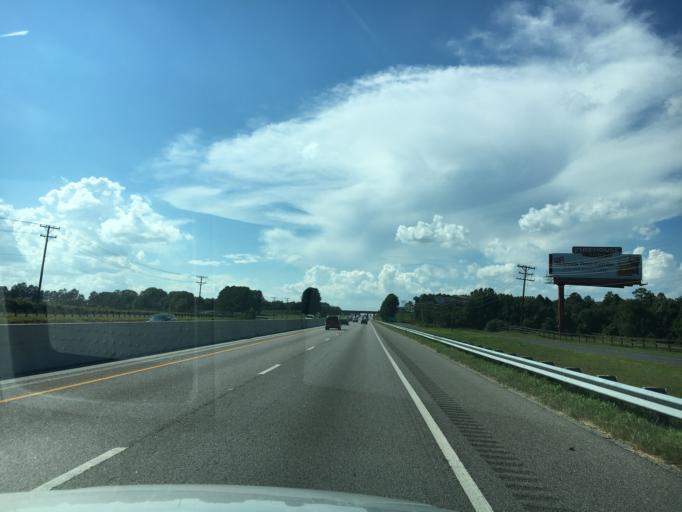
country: US
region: South Carolina
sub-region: Greenville County
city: Fountain Inn
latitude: 34.6859
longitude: -82.2133
